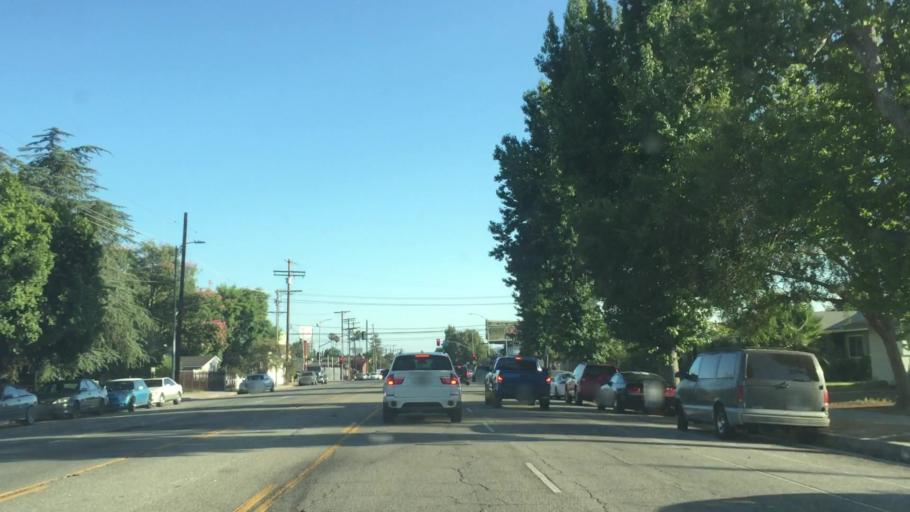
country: US
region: California
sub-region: Los Angeles County
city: Northridge
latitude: 34.2370
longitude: -118.4851
